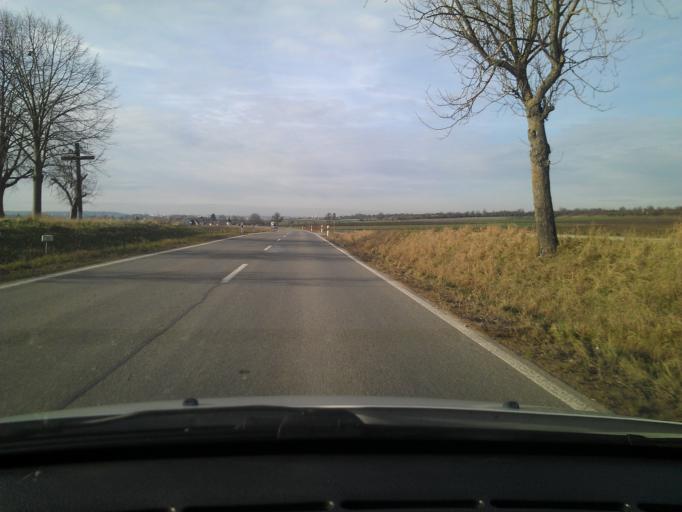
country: DE
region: Baden-Wuerttemberg
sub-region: Regierungsbezirk Stuttgart
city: Neuhausen auf den Fildern
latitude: 48.6895
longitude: 9.2905
